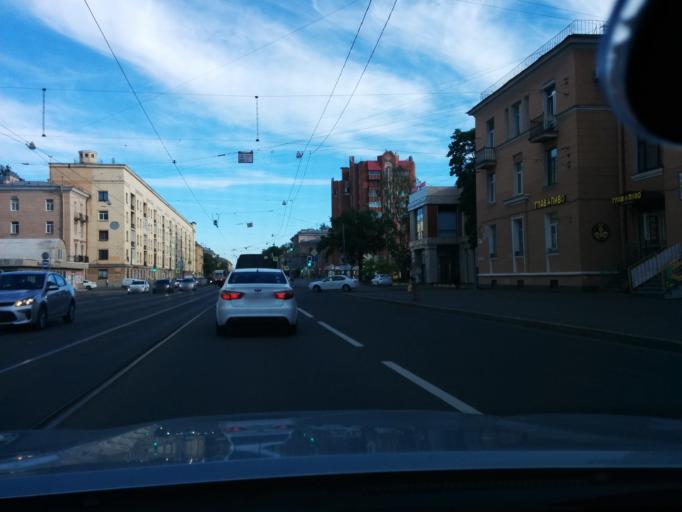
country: RU
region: Leningrad
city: Udel'naya
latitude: 60.0182
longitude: 30.3217
